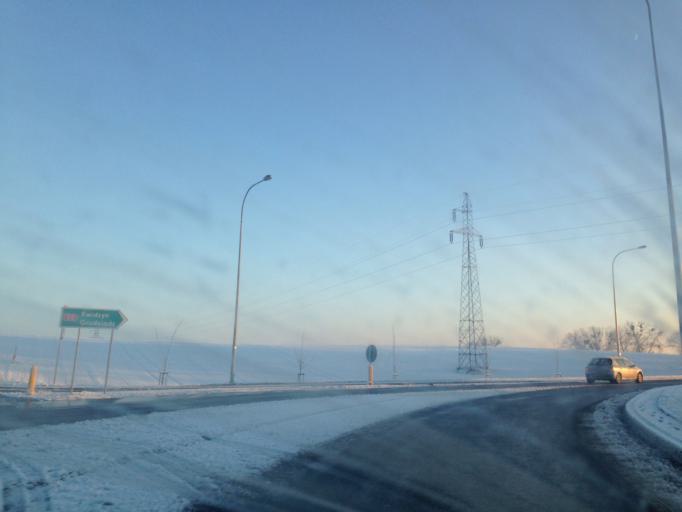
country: PL
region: Pomeranian Voivodeship
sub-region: Powiat kwidzynski
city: Kwidzyn
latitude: 53.7555
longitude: 18.9405
